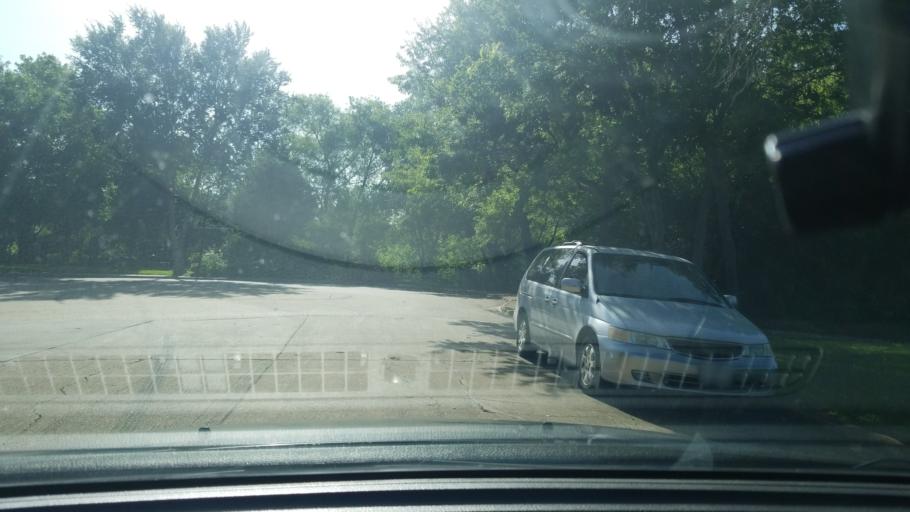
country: US
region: Texas
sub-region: Dallas County
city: Mesquite
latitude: 32.8107
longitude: -96.6740
